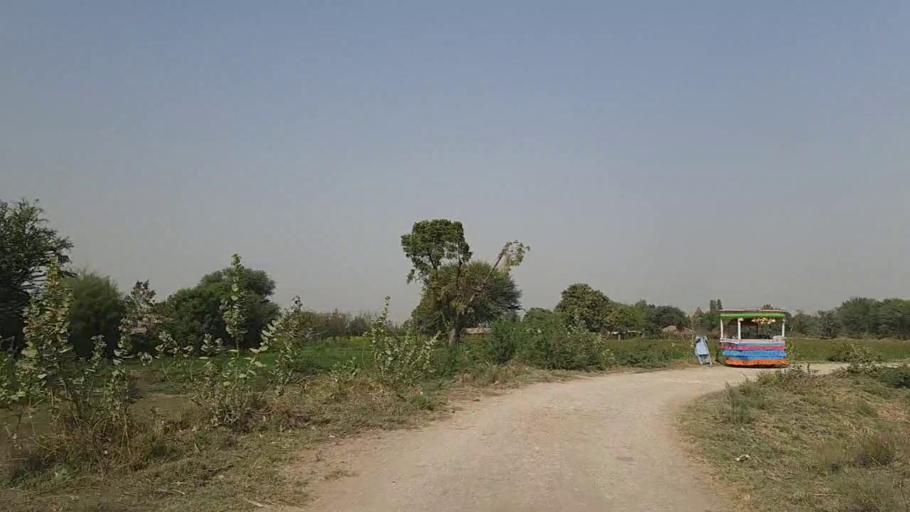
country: PK
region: Sindh
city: Samaro
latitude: 25.2829
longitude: 69.3734
